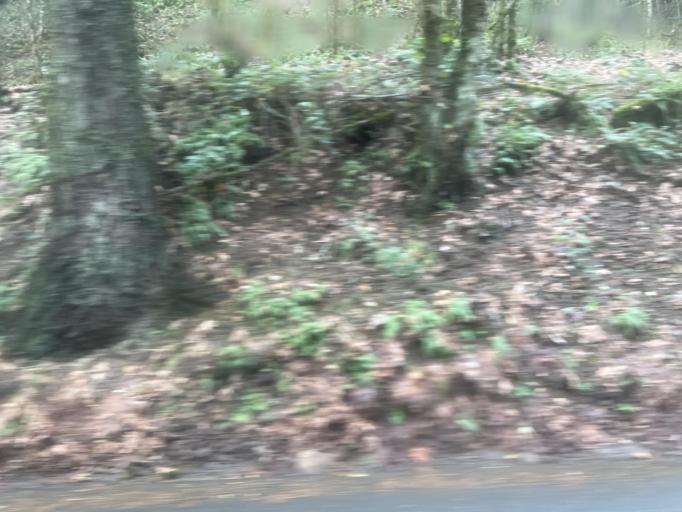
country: US
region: Washington
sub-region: Clark County
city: Washougal
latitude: 45.5523
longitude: -122.1860
